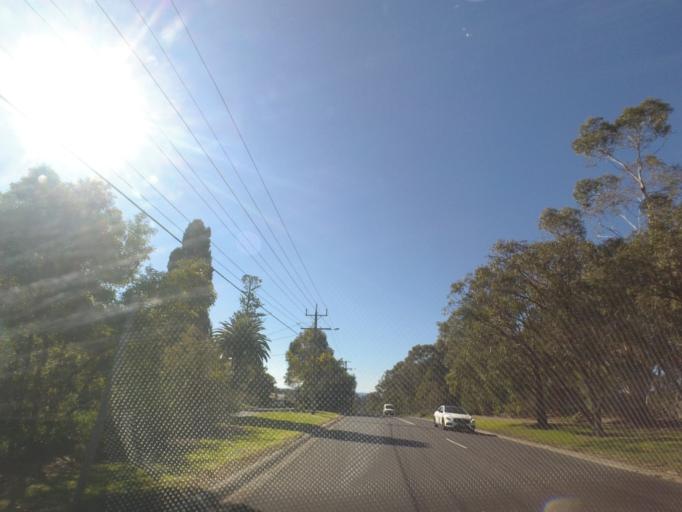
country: AU
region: Victoria
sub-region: Maroondah
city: Croydon Hills
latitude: -37.7776
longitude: 145.2749
